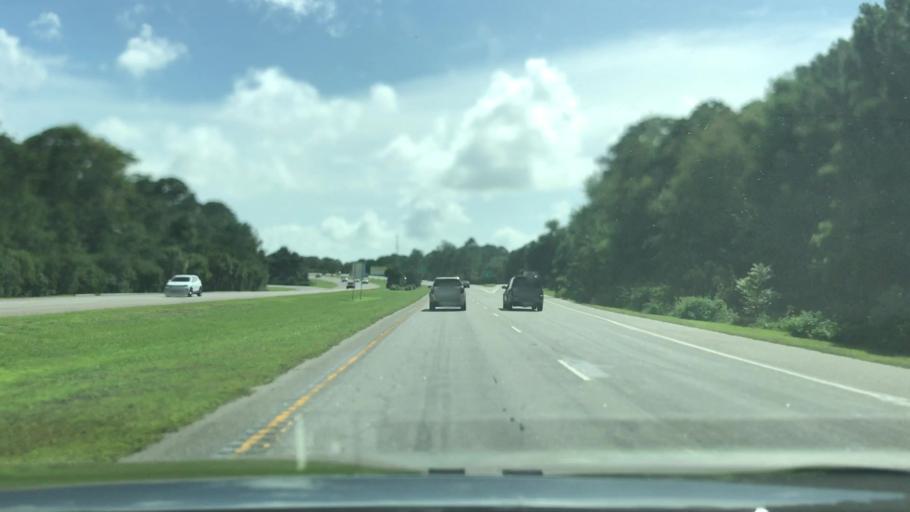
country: US
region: South Carolina
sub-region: Beaufort County
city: Hilton Head Island
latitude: 32.1967
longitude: -80.7603
